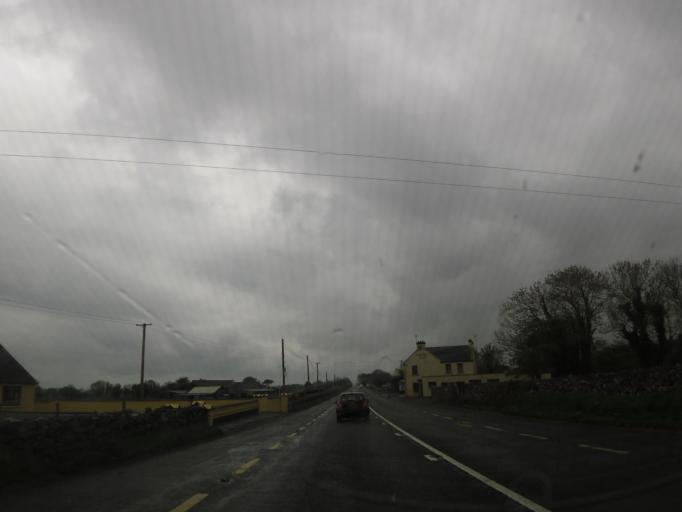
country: IE
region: Connaught
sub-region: County Galway
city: Claregalway
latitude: 53.4266
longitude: -8.9022
